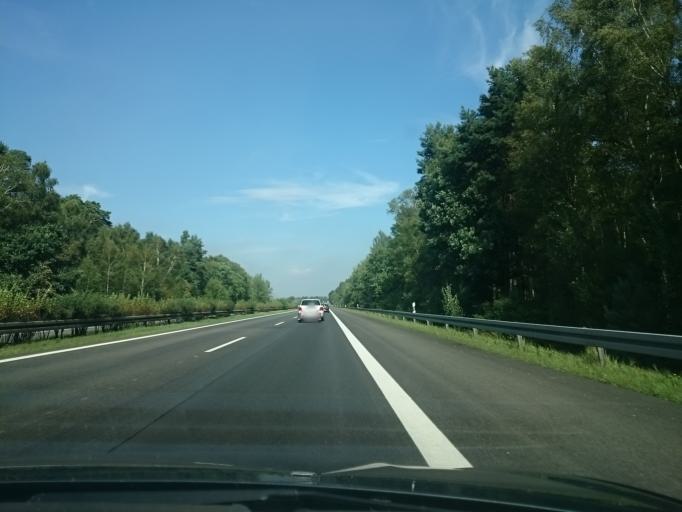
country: DE
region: Brandenburg
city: Bronkow
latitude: 51.6172
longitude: 13.9485
